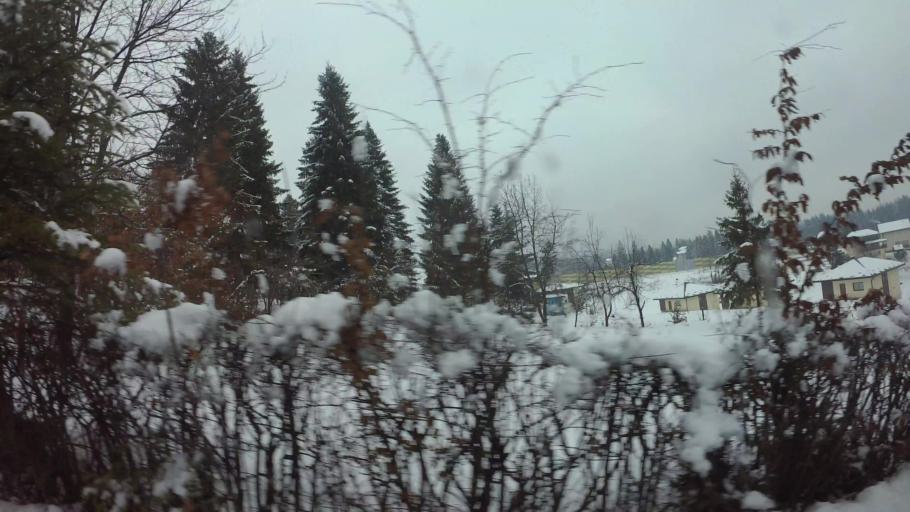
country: BA
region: Federation of Bosnia and Herzegovina
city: Hadzici
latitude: 43.8602
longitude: 18.2654
